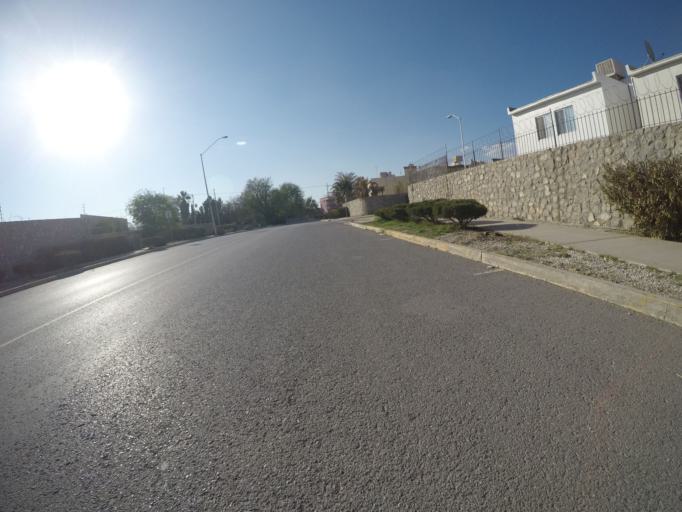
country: MX
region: Chihuahua
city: Ciudad Juarez
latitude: 31.7034
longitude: -106.3972
